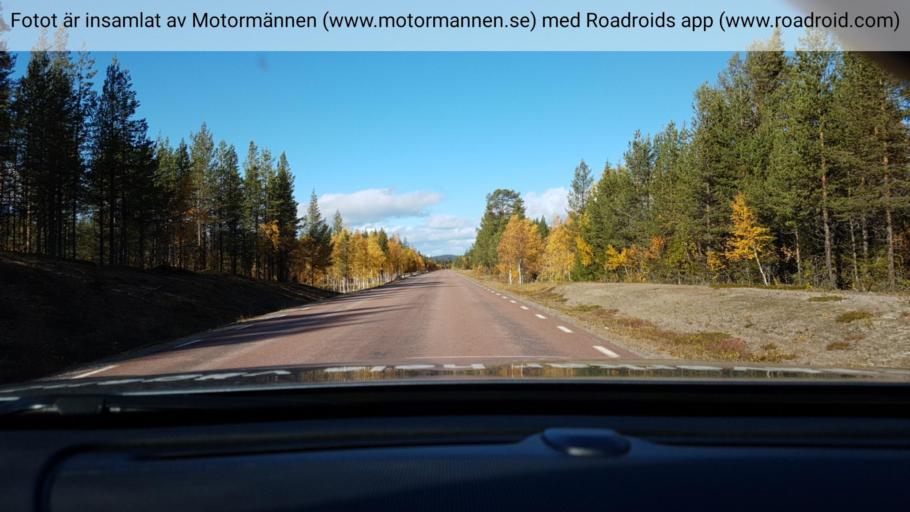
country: SE
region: Norrbotten
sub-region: Arjeplogs Kommun
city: Arjeplog
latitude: 66.0061
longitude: 18.1078
